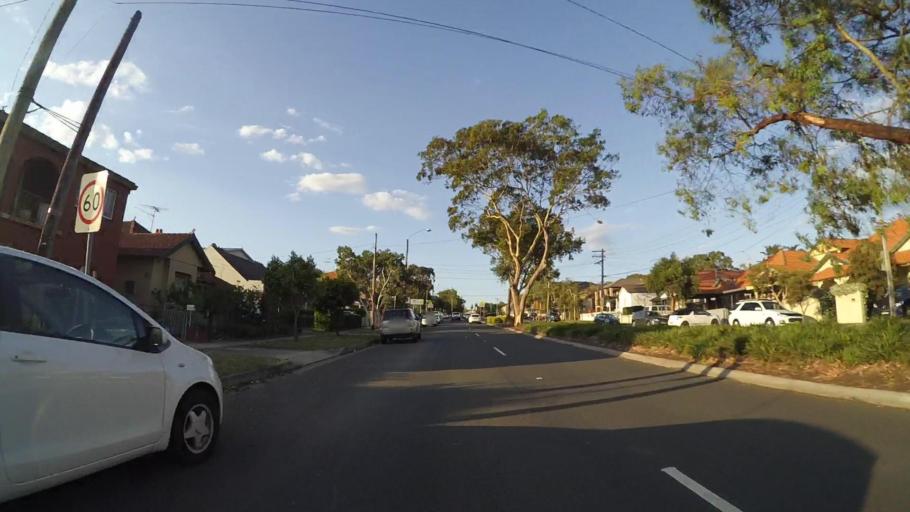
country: AU
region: New South Wales
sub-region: Randwick
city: Daceyville
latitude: -33.9267
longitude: 151.2390
